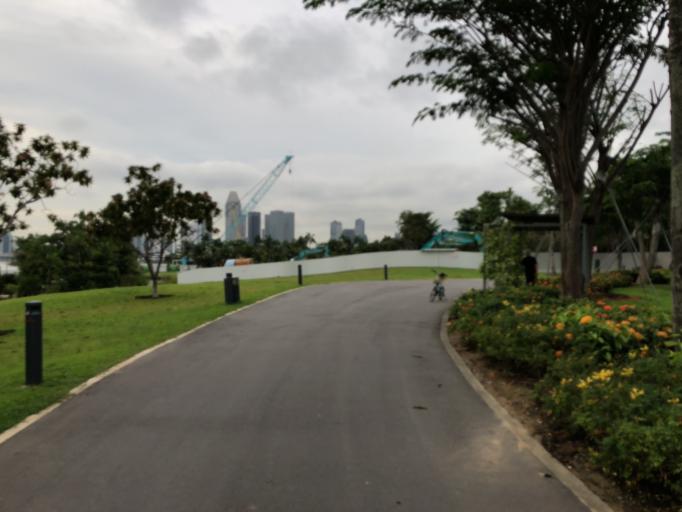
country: SG
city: Singapore
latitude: 1.2837
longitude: 103.8734
